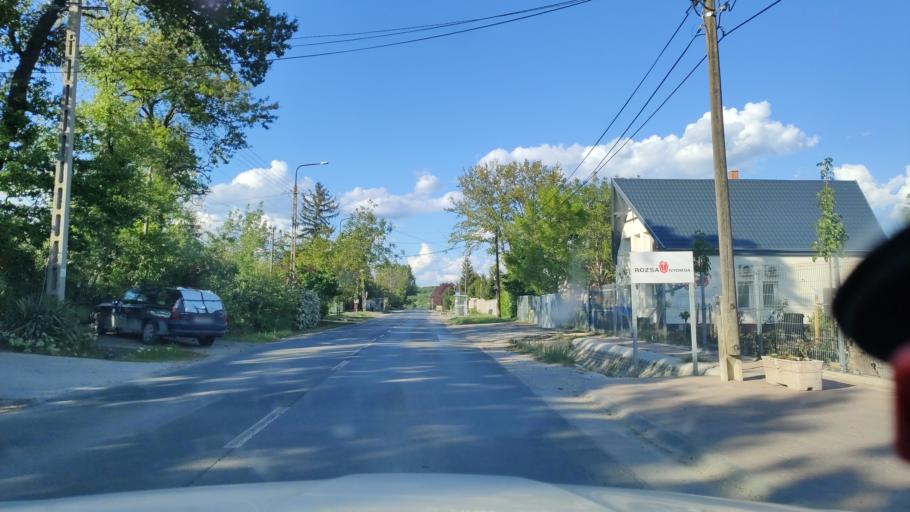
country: HU
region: Pest
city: Toeroekbalint
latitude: 47.4153
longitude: 18.8892
